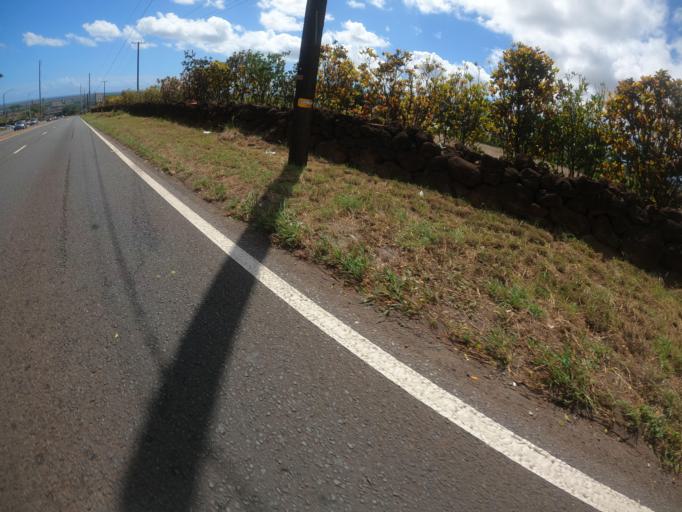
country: US
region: Hawaii
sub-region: Honolulu County
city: Royal Kunia
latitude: 21.3876
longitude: -158.0342
